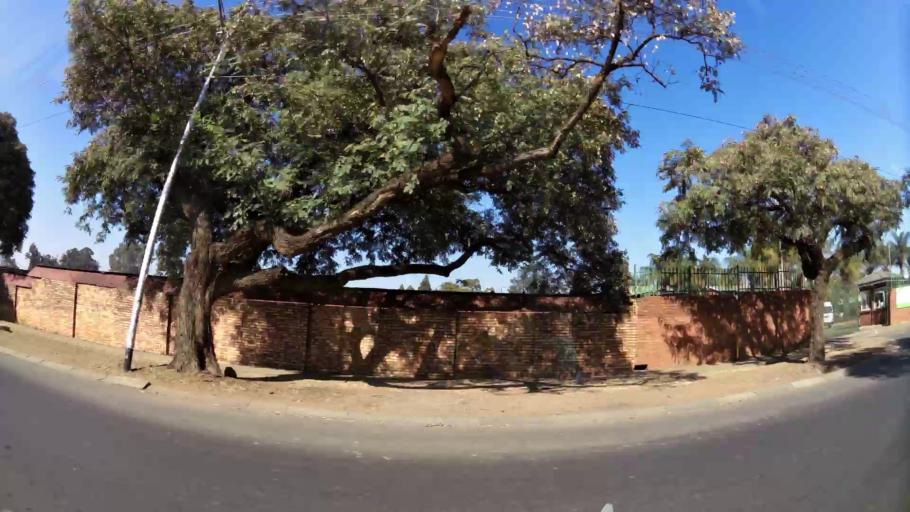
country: ZA
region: Gauteng
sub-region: City of Tshwane Metropolitan Municipality
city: Pretoria
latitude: -25.7444
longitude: 28.1751
